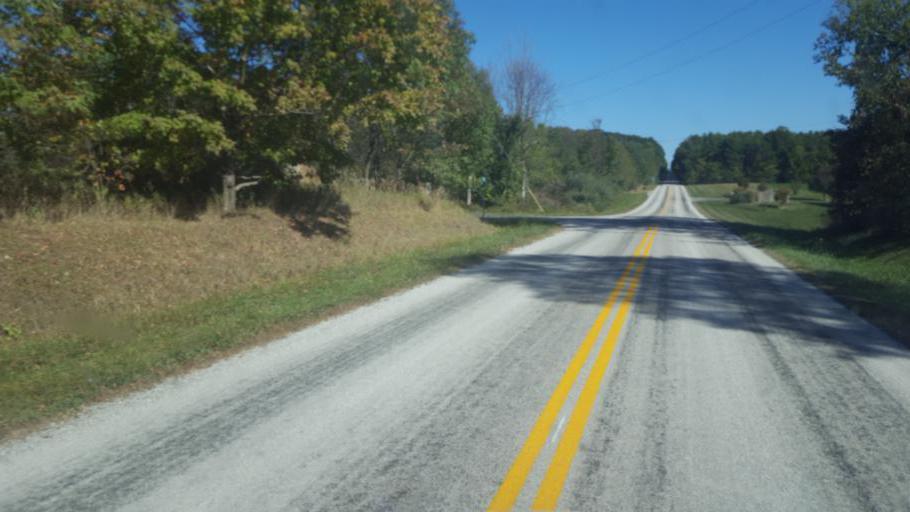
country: US
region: Ohio
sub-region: Wayne County
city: West Salem
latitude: 40.9926
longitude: -82.2431
